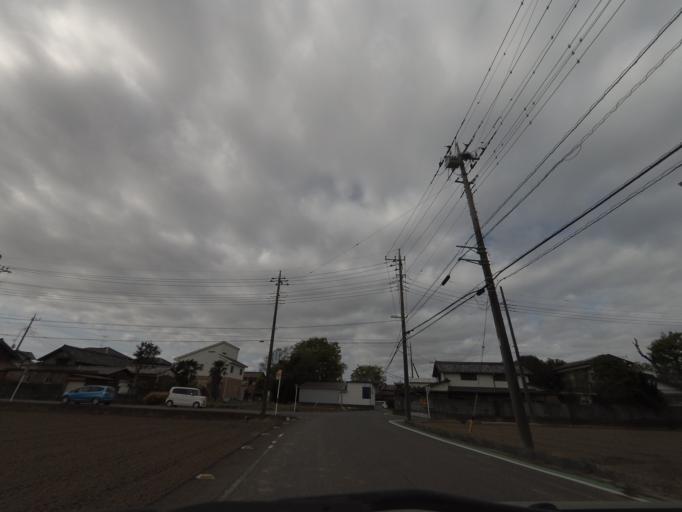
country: JP
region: Saitama
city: Kamifukuoka
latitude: 35.8902
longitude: 139.5464
